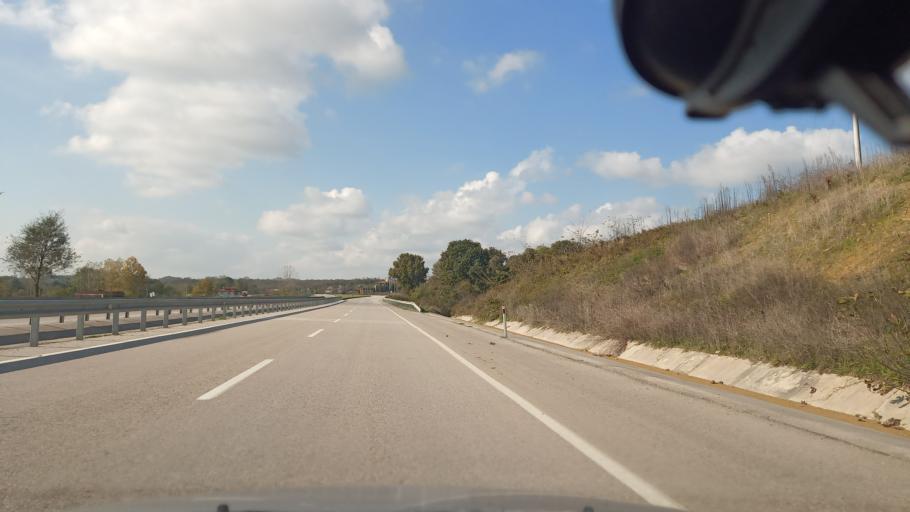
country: TR
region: Sakarya
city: Kaynarca
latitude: 41.0722
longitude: 30.3806
